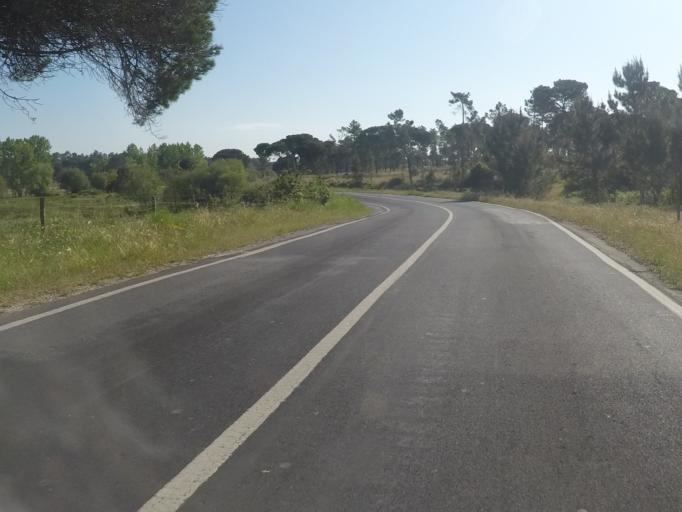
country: PT
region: Setubal
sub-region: Sesimbra
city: Sesimbra
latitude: 38.5299
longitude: -9.1274
